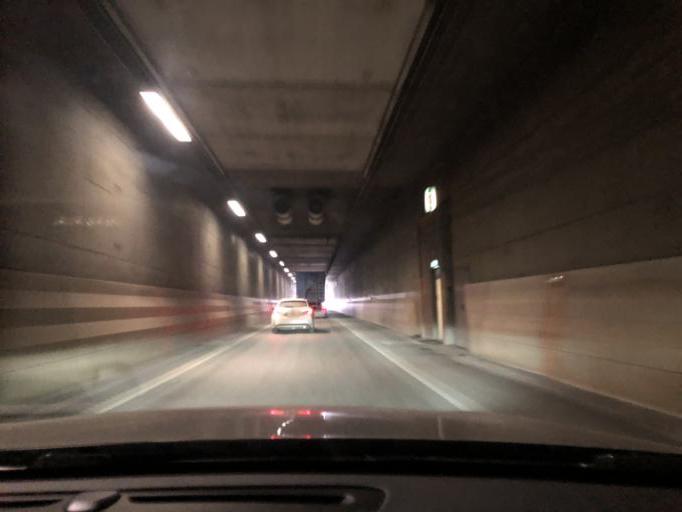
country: SE
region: Stockholm
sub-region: Stockholms Kommun
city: Arsta
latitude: 59.2911
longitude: 18.0809
